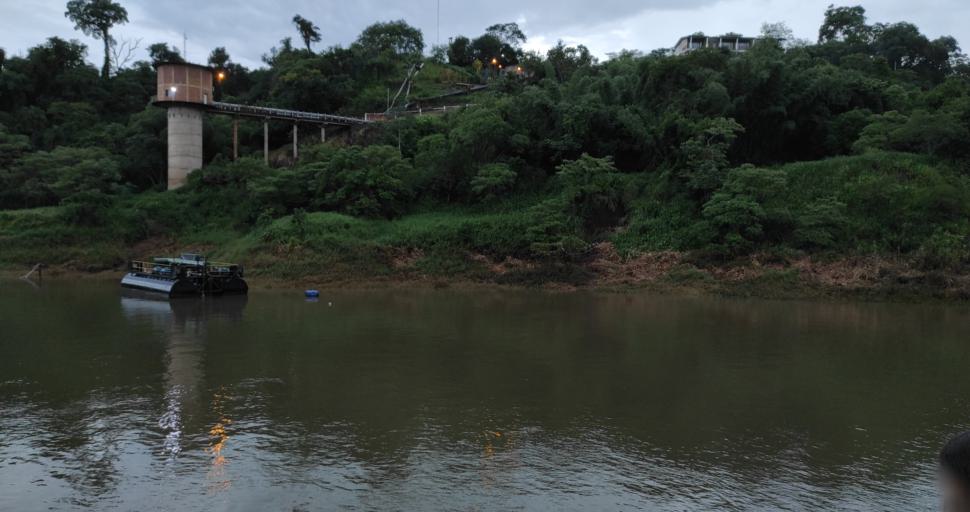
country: AR
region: Misiones
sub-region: Departamento de Iguazu
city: Puerto Iguazu
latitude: -25.5911
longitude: -54.5656
